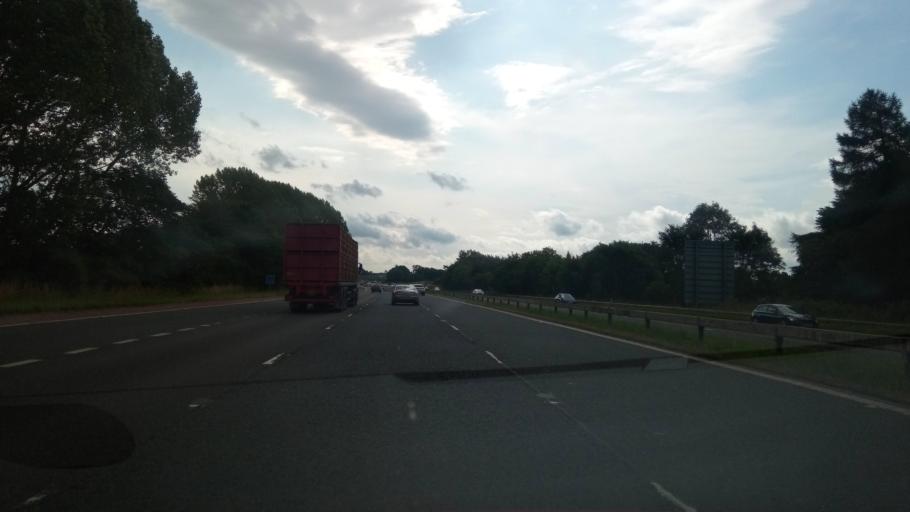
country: GB
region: England
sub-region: Cumbria
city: Penrith
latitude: 54.6502
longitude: -2.7541
